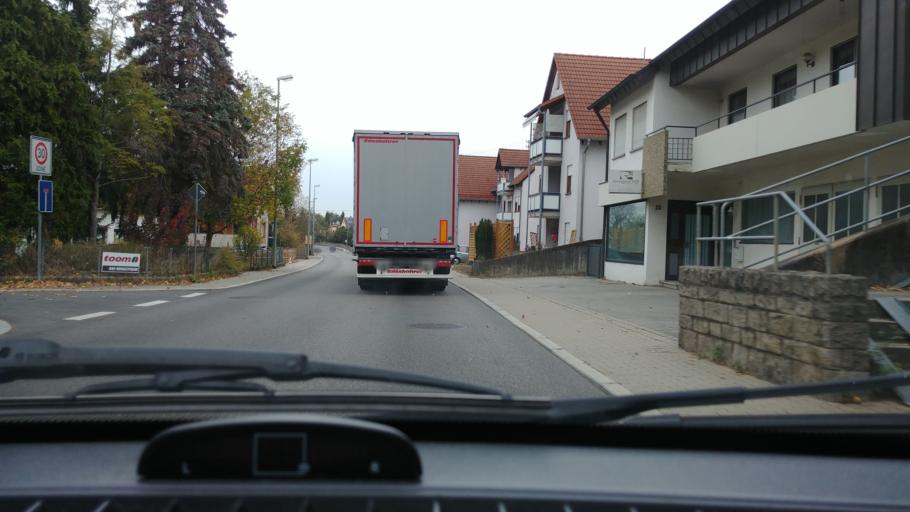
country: DE
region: Baden-Wuerttemberg
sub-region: Regierungsbezirk Stuttgart
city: Bad Mergentheim
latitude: 49.5135
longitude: 9.7520
